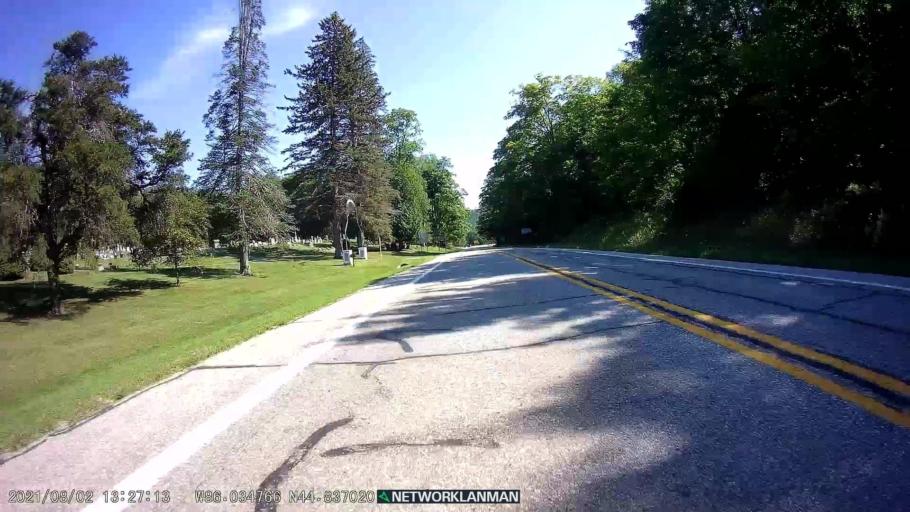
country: US
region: Michigan
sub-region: Benzie County
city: Beulah
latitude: 44.8371
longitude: -86.0348
